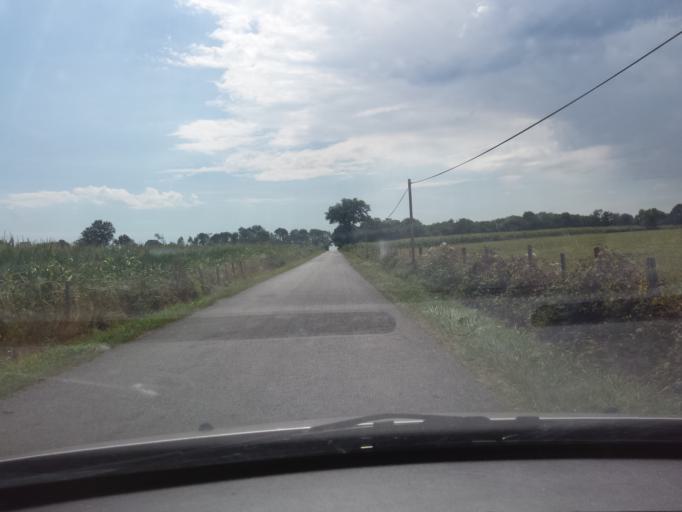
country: FR
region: Poitou-Charentes
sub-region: Departement de la Vienne
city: Availles-Limouzine
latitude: 46.0816
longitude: 0.7410
